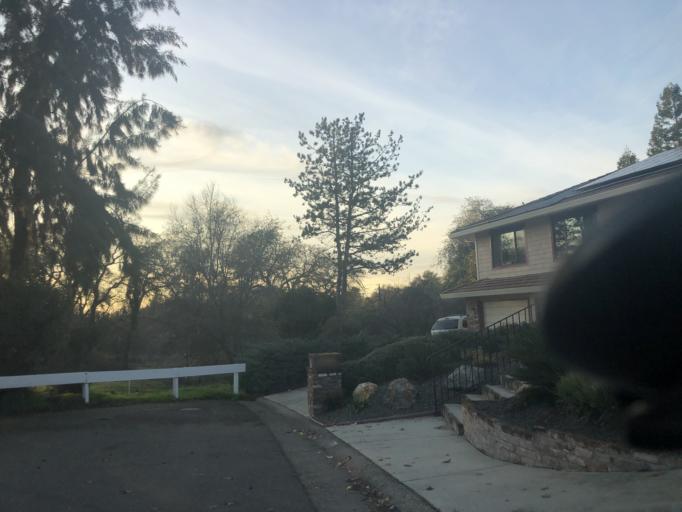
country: US
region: California
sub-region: Sacramento County
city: Gold River
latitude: 38.6413
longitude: -121.2334
